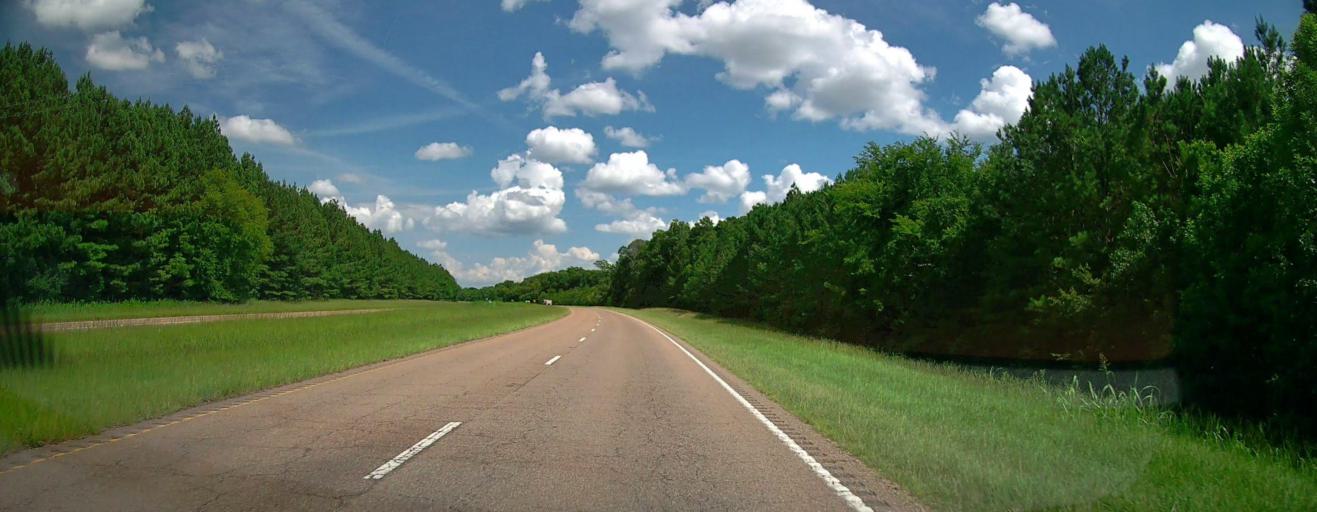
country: US
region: Mississippi
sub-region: Monroe County
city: Aberdeen
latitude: 33.8170
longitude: -88.5782
